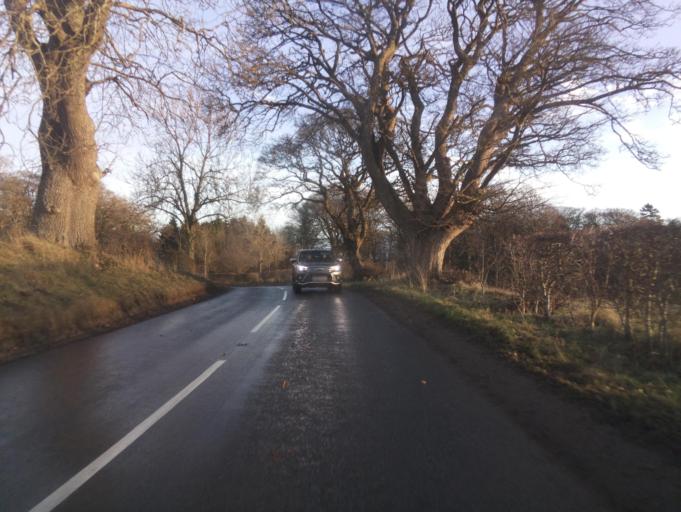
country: GB
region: Scotland
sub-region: Angus
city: Forfar
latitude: 56.5875
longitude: -2.8877
